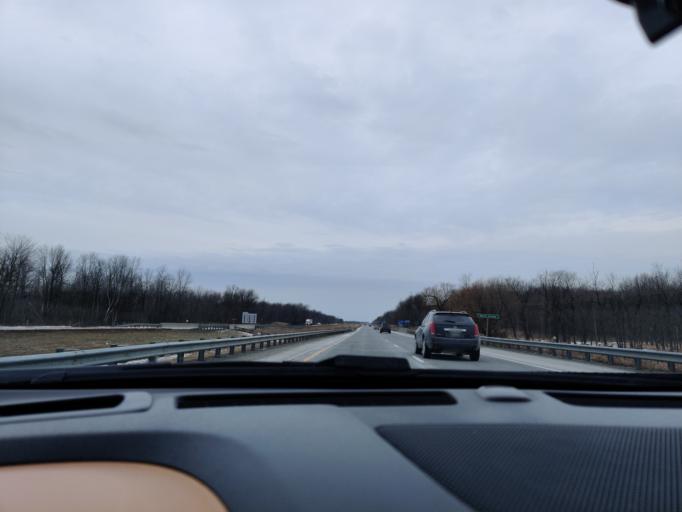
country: US
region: New York
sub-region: St. Lawrence County
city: Norfolk
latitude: 44.9312
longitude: -75.1651
